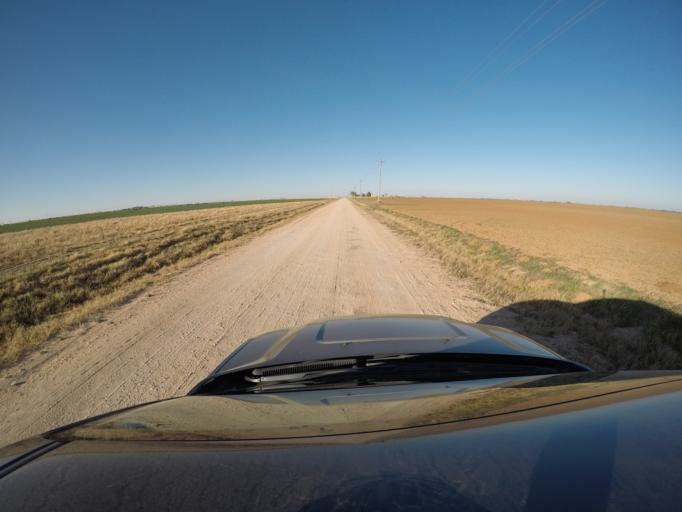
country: US
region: New Mexico
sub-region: Curry County
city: Texico
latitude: 34.3772
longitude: -103.1082
